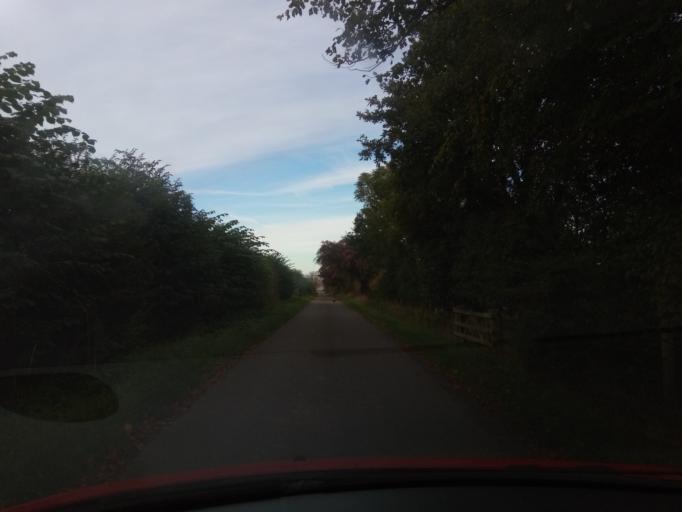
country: GB
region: Scotland
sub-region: The Scottish Borders
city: Jedburgh
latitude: 55.4828
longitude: -2.4987
